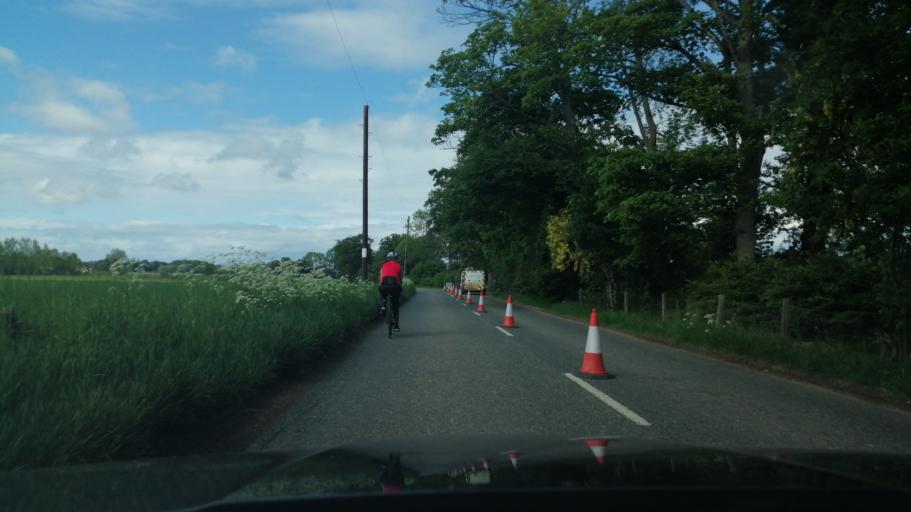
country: GB
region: Scotland
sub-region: Moray
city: Lhanbryd
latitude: 57.6430
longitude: -3.2474
